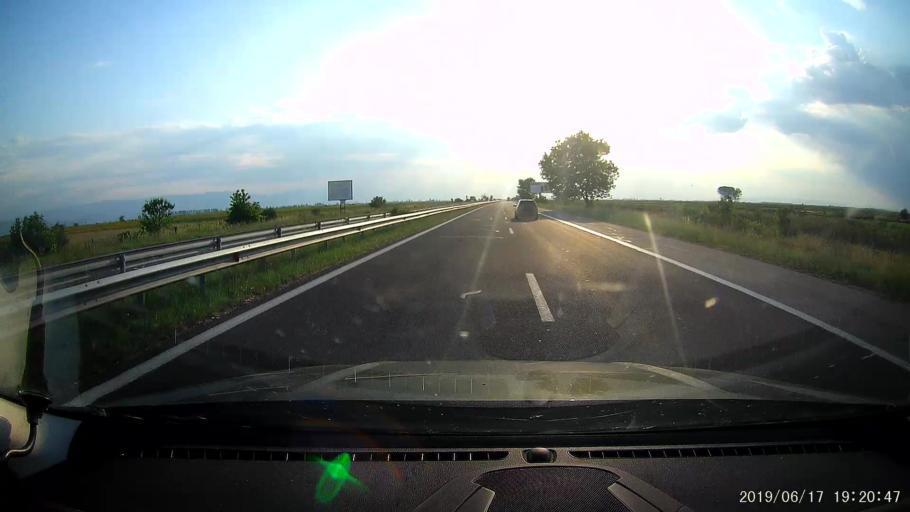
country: BG
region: Plovdiv
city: Stamboliyski
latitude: 42.2060
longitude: 24.4838
